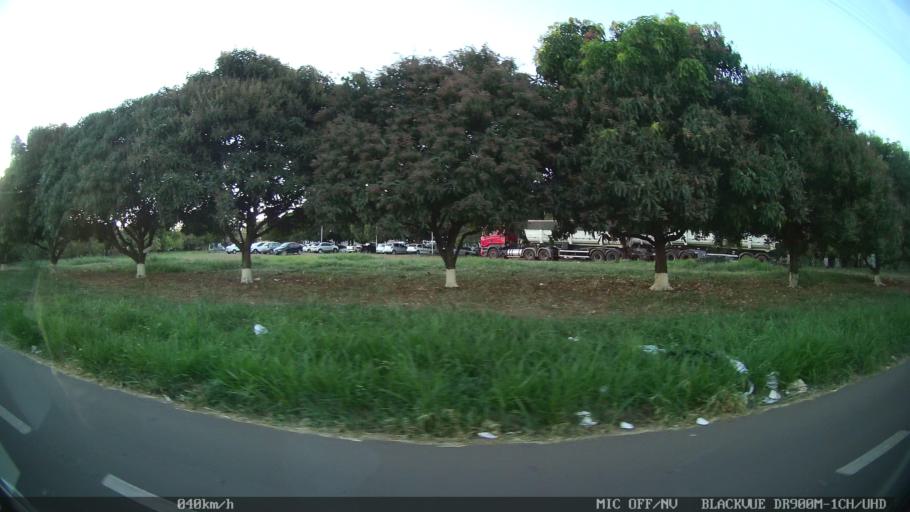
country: BR
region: Sao Paulo
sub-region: Sao Jose Do Rio Preto
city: Sao Jose do Rio Preto
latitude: -20.8439
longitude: -49.3807
